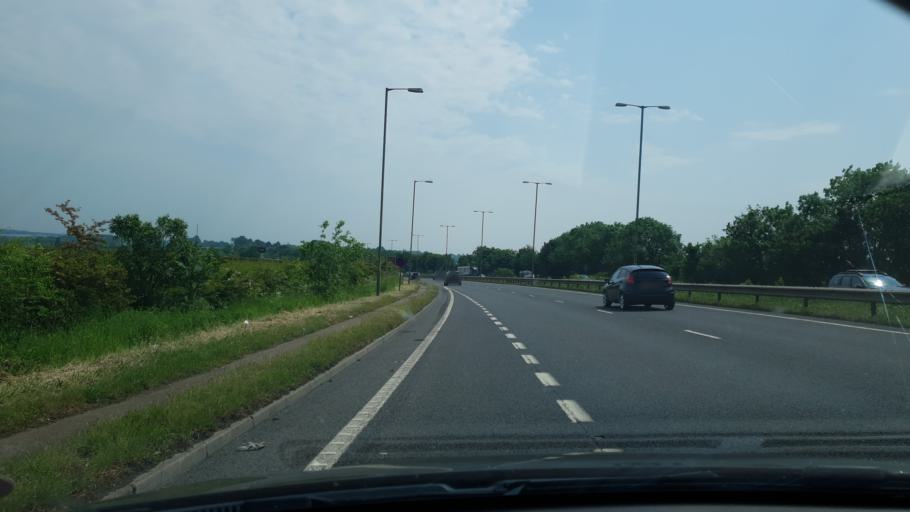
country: GB
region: England
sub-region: Northamptonshire
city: Rothwell
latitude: 52.4133
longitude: -0.7861
